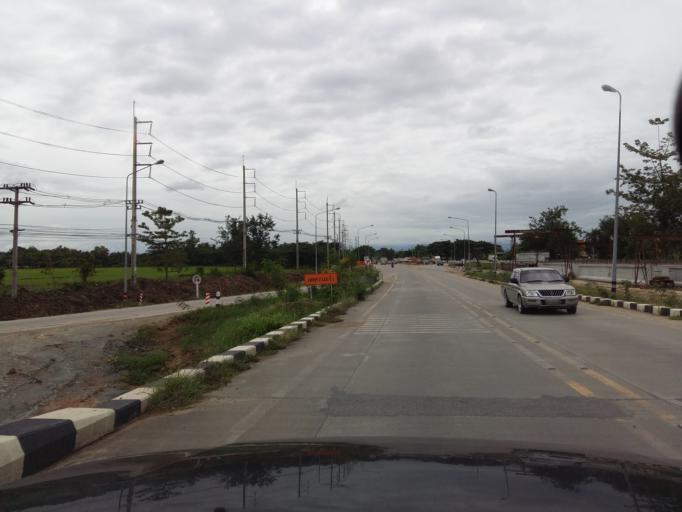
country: TH
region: Chiang Mai
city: Saraphi
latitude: 18.7367
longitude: 99.0396
